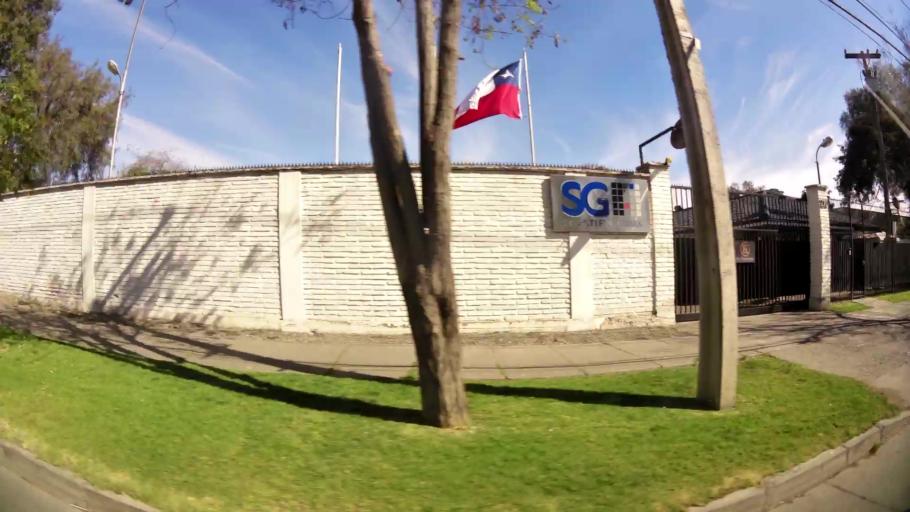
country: CL
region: Santiago Metropolitan
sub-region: Provincia de Santiago
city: Lo Prado
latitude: -33.4845
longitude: -70.7003
